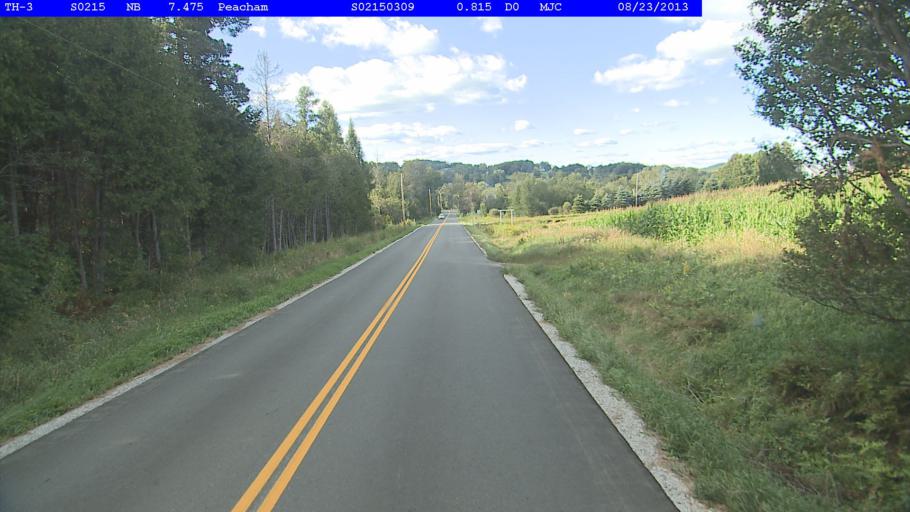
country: US
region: Vermont
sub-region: Caledonia County
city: Saint Johnsbury
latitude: 44.3095
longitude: -72.1658
